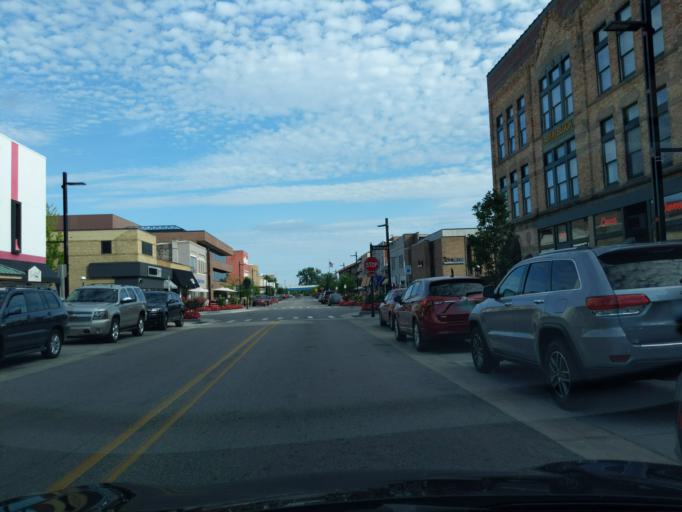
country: US
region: Michigan
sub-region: Midland County
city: Midland
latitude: 43.6129
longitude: -84.2452
